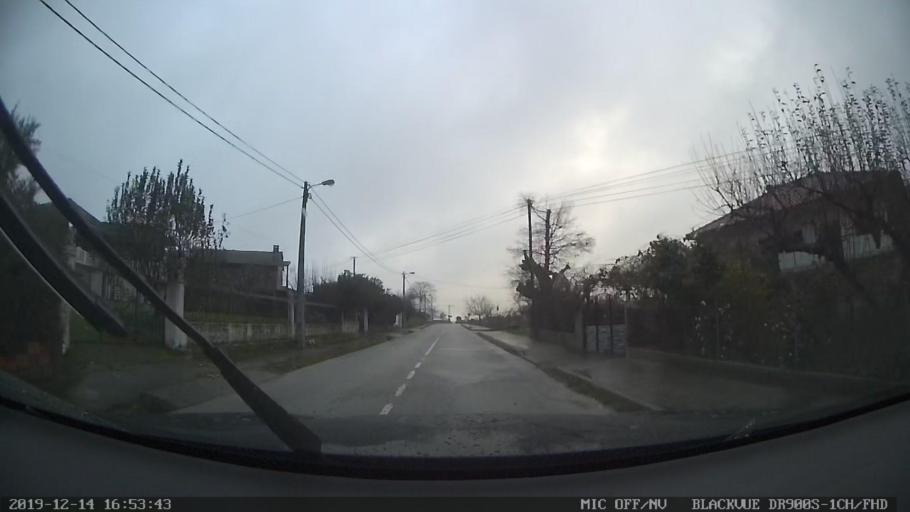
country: PT
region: Vila Real
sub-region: Murca
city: Murca
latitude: 41.4334
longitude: -7.5185
